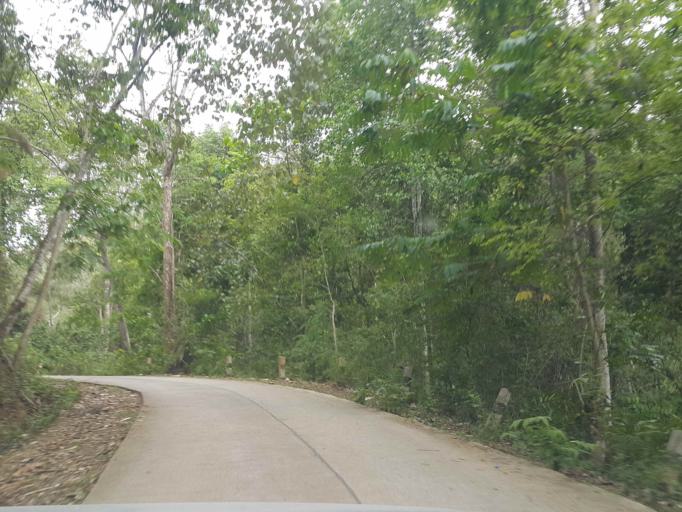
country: TH
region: Chiang Mai
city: Wiang Haeng
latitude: 19.3761
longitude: 98.7514
